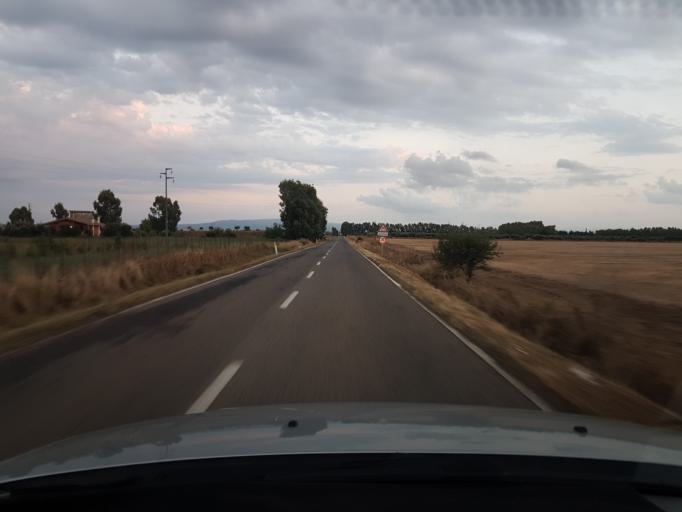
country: IT
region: Sardinia
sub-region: Provincia di Oristano
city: Milis
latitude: 40.0271
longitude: 8.6406
